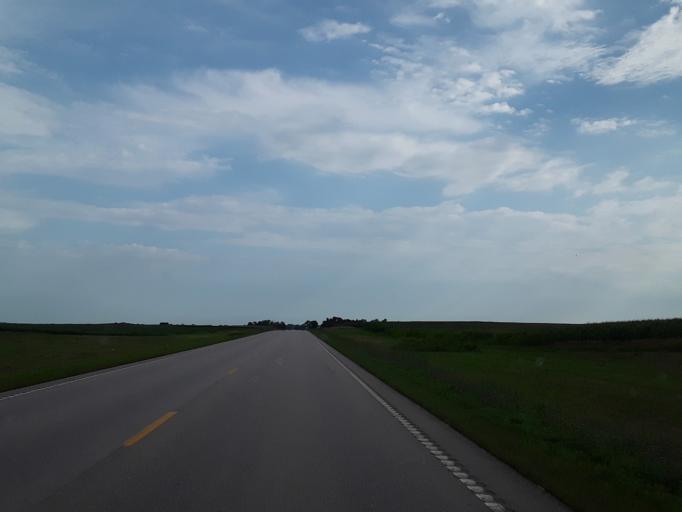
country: US
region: Nebraska
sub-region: Saunders County
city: Ashland
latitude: 41.1104
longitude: -96.4258
